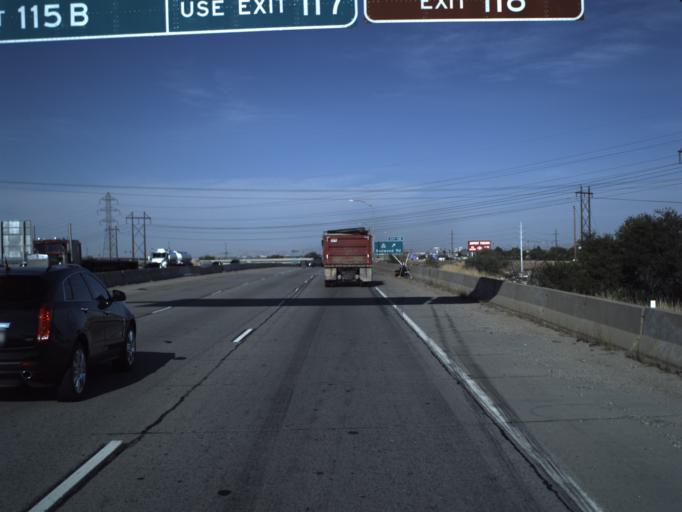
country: US
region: Utah
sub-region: Salt Lake County
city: Salt Lake City
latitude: 40.7655
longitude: -111.9329
